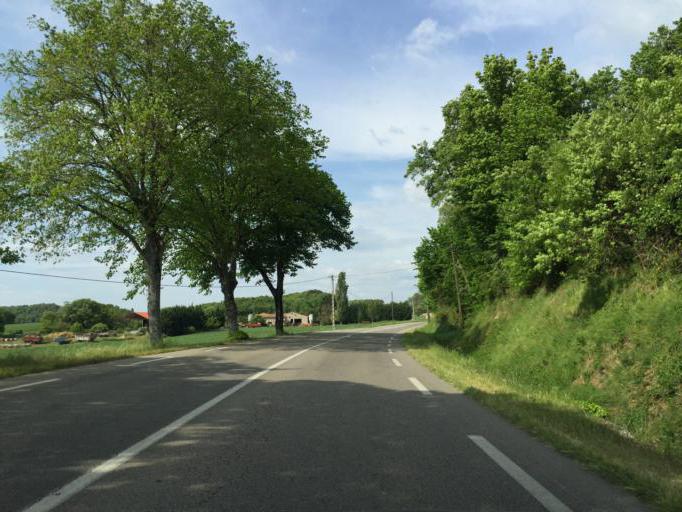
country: FR
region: Rhone-Alpes
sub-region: Departement de la Drome
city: Eurre
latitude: 44.7790
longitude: 5.0219
